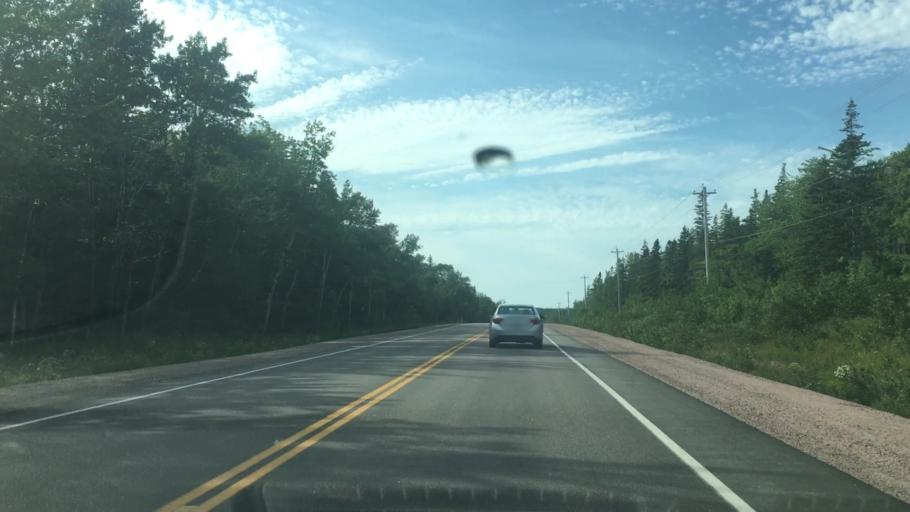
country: CA
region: Nova Scotia
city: Sydney Mines
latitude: 46.8193
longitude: -60.3507
